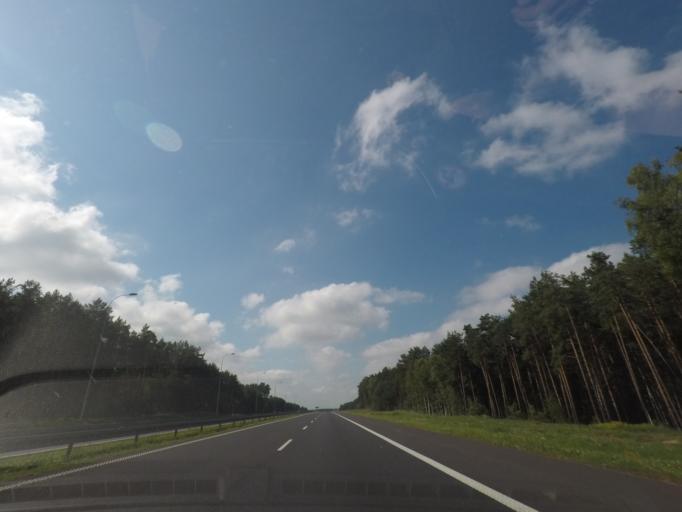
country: PL
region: Kujawsko-Pomorskie
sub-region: Powiat swiecki
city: Warlubie
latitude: 53.6283
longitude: 18.6389
